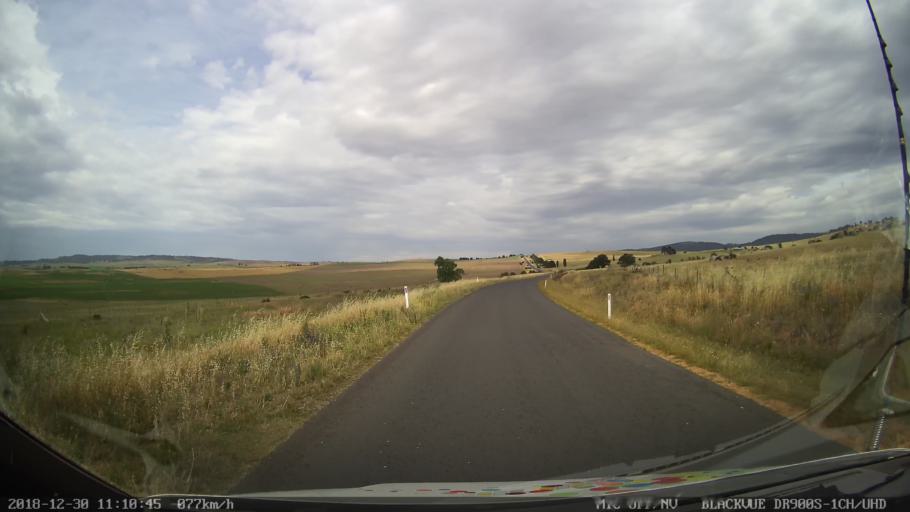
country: AU
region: New South Wales
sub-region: Snowy River
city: Berridale
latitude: -36.5171
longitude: 148.7781
